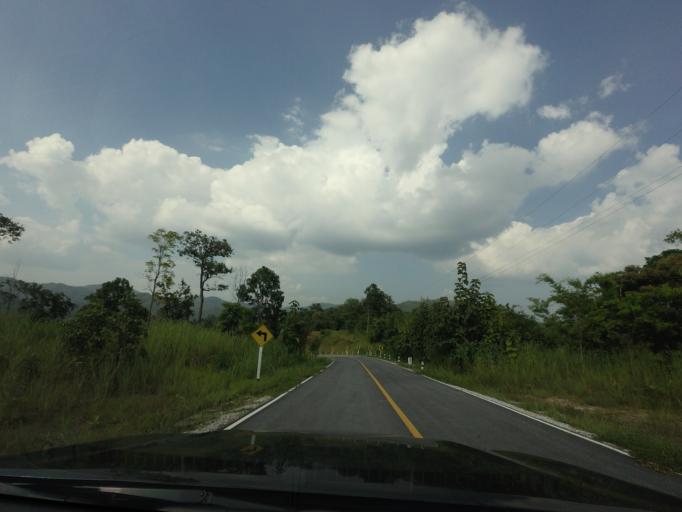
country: TH
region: Uttaradit
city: Ban Khok
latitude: 18.2284
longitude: 101.0332
